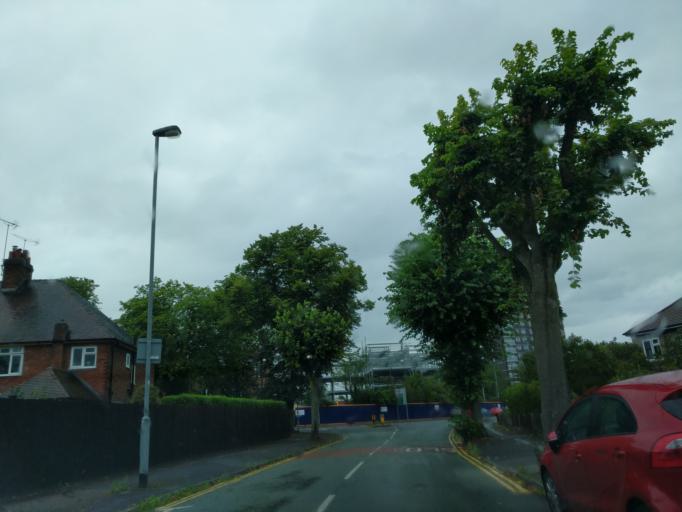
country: GB
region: England
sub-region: Staffordshire
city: Stafford
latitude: 52.8053
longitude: -2.1045
